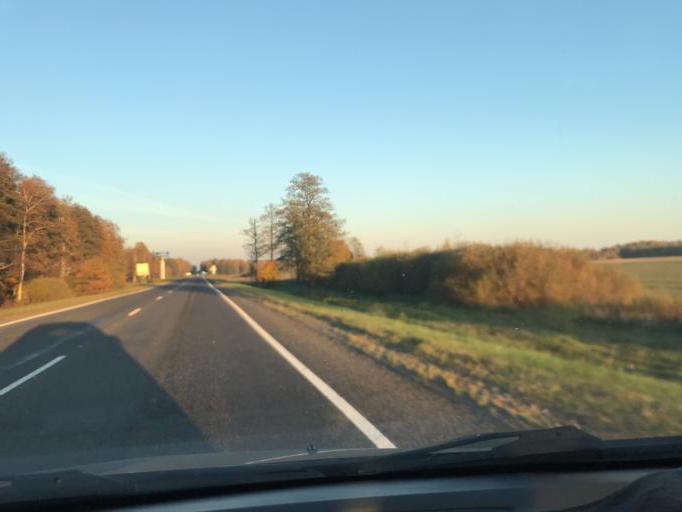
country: BY
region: Mogilev
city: Hlusk
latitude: 53.0640
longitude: 28.5242
